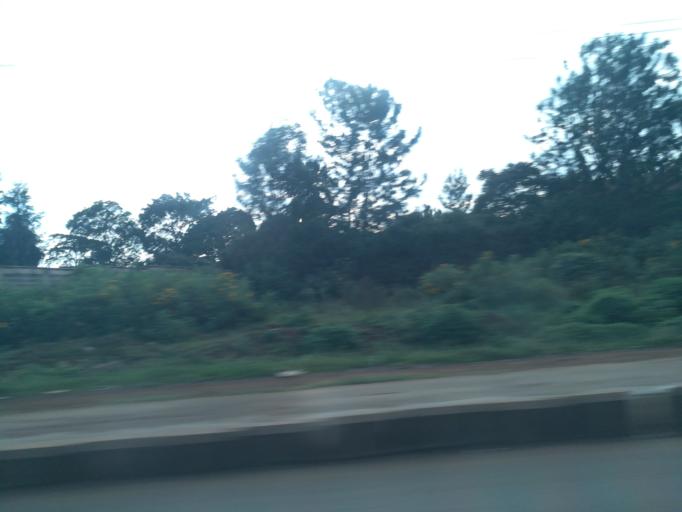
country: KE
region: Nairobi Area
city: Thika
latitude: -1.1108
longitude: 37.0125
